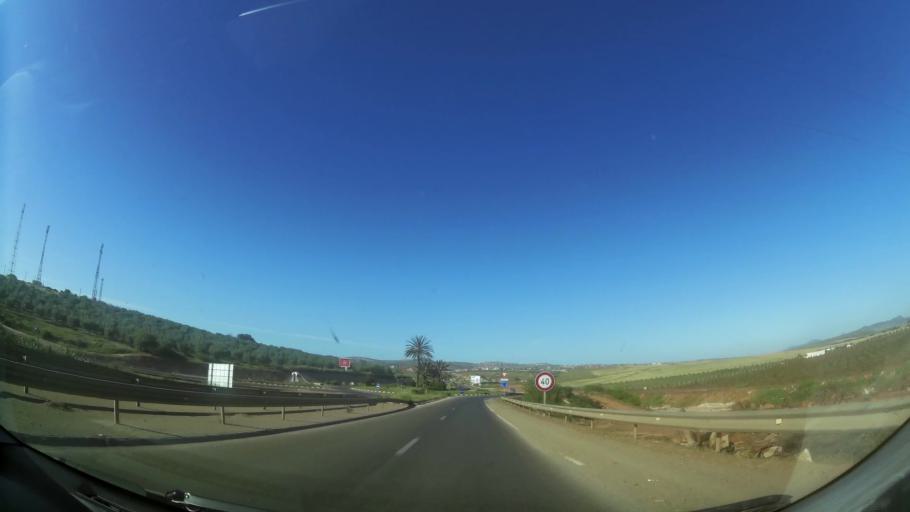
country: MA
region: Oriental
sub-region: Berkane-Taourirt
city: Ahfir
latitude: 35.0298
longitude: -2.2050
